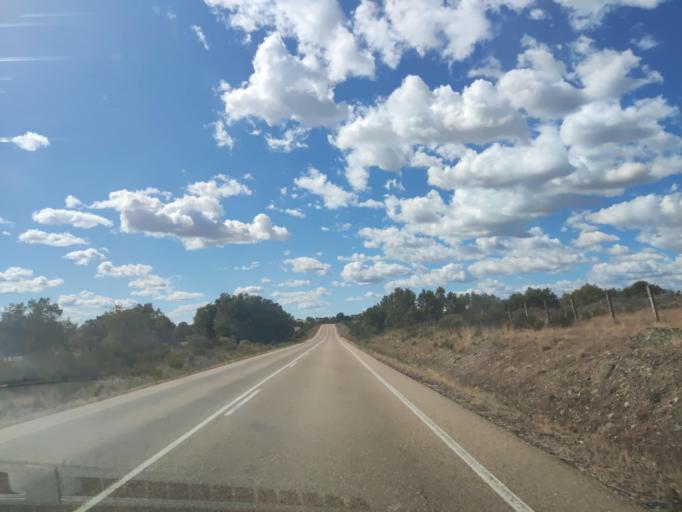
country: ES
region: Castille and Leon
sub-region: Provincia de Salamanca
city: Moronta
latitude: 40.9721
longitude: -6.3966
